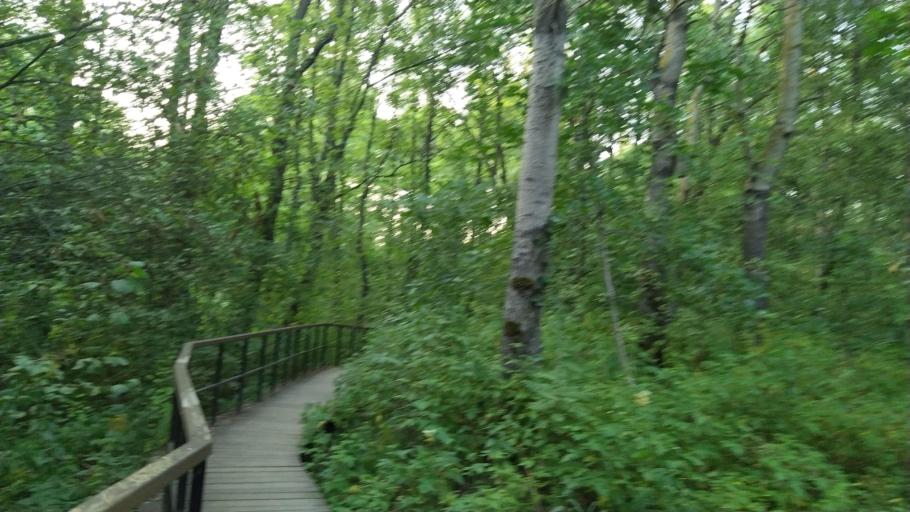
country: RU
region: St.-Petersburg
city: Kronshtadt
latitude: 60.0255
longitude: 29.6721
